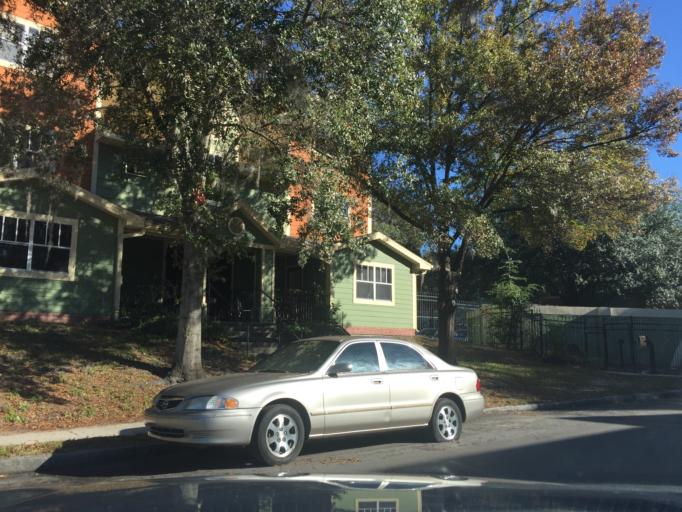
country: US
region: Florida
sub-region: Hillsborough County
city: Tampa
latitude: 27.9595
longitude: -82.4573
